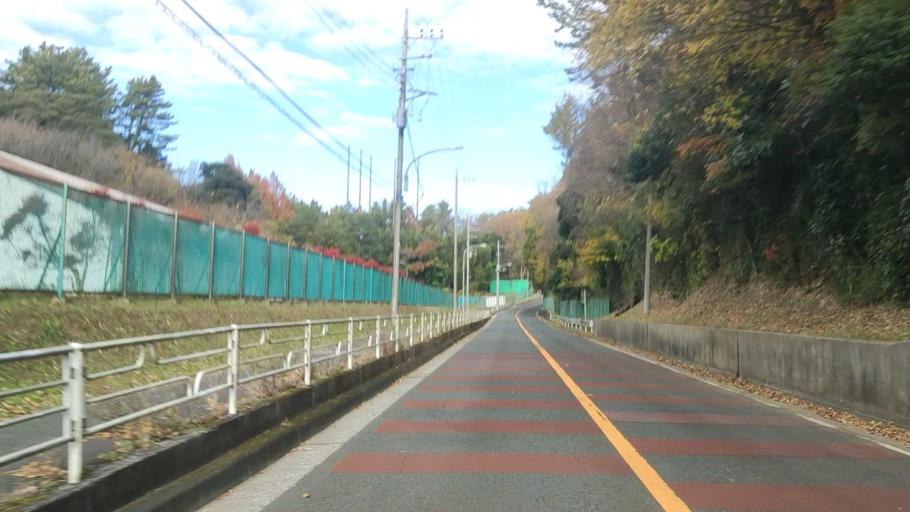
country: JP
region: Kanagawa
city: Yokohama
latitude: 35.4410
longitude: 139.5443
